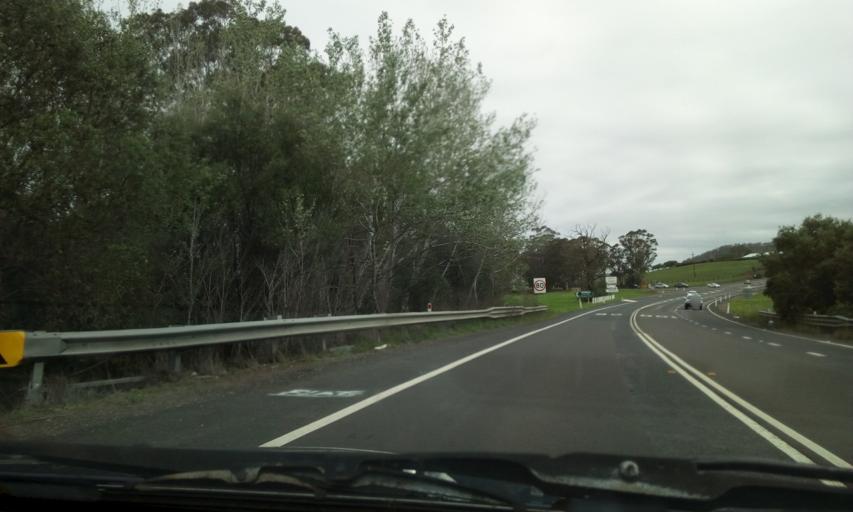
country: AU
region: New South Wales
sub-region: Camden
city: Camden South
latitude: -34.1197
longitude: 150.6990
